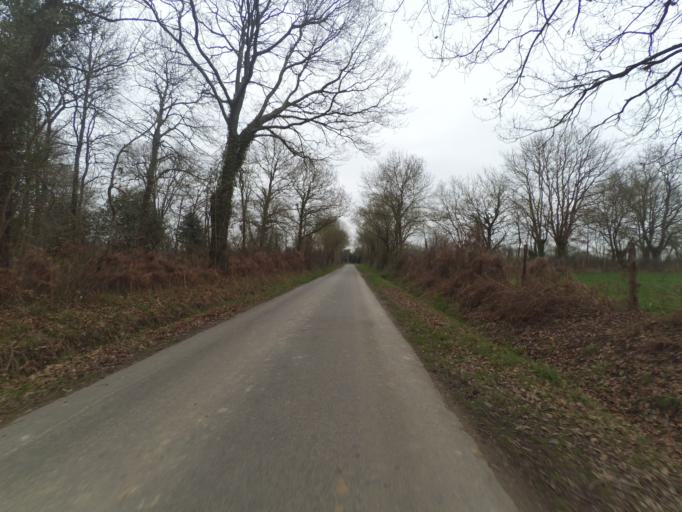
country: FR
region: Pays de la Loire
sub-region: Departement de la Loire-Atlantique
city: Coueron
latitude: 47.2392
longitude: -1.7079
